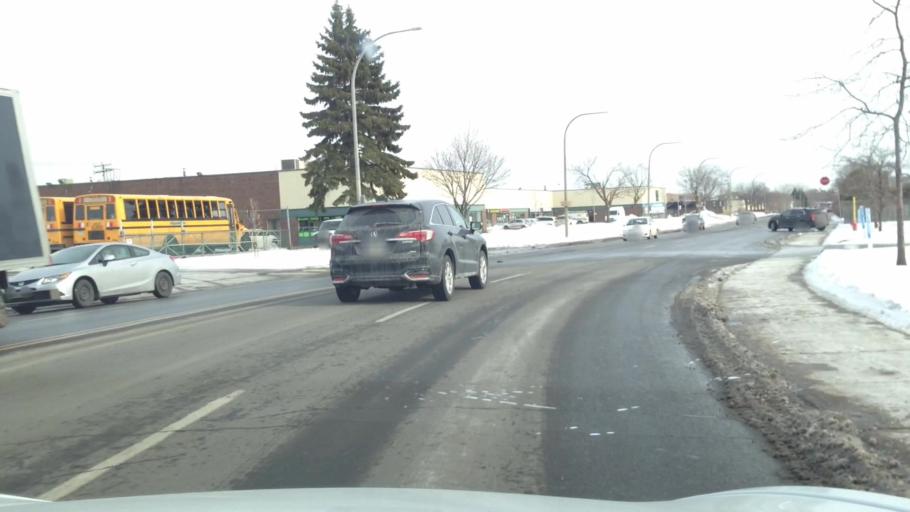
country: CA
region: Quebec
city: Kirkland
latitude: 45.4498
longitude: -73.8547
